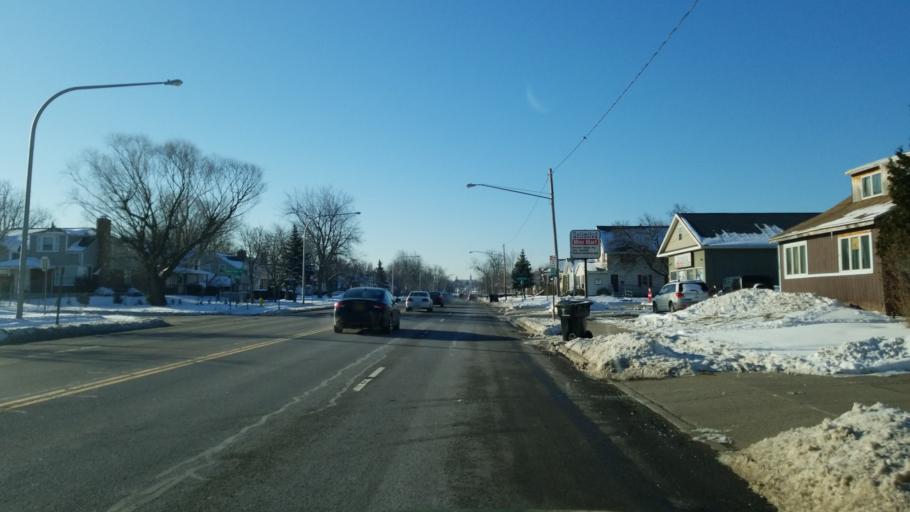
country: US
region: New York
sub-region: Erie County
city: Eggertsville
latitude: 42.9643
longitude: -78.8236
